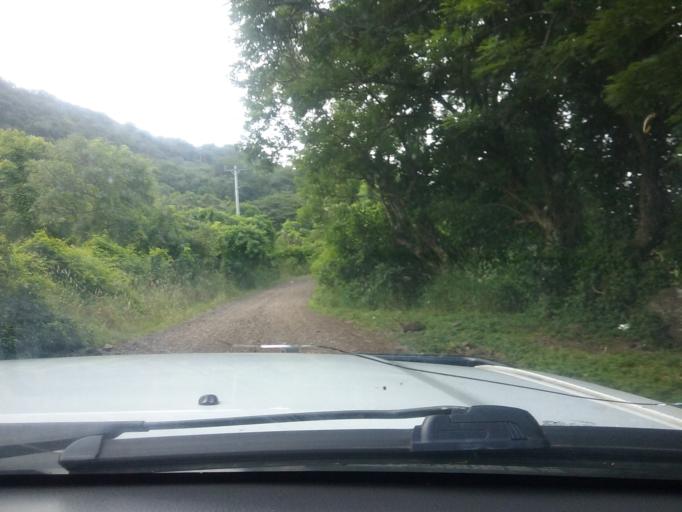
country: NI
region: Matagalpa
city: Matagalpa
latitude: 12.8797
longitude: -85.9595
